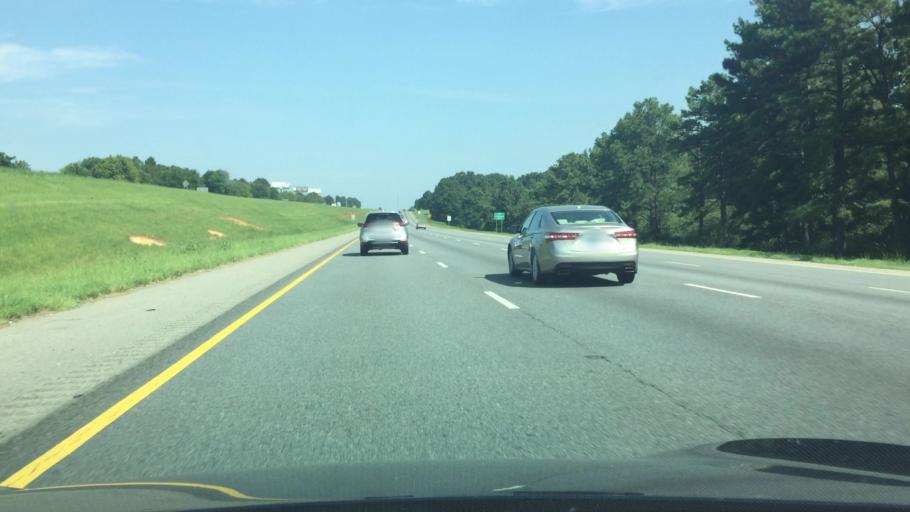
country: US
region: Alabama
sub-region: Elmore County
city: Millbrook
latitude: 32.4918
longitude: -86.4113
